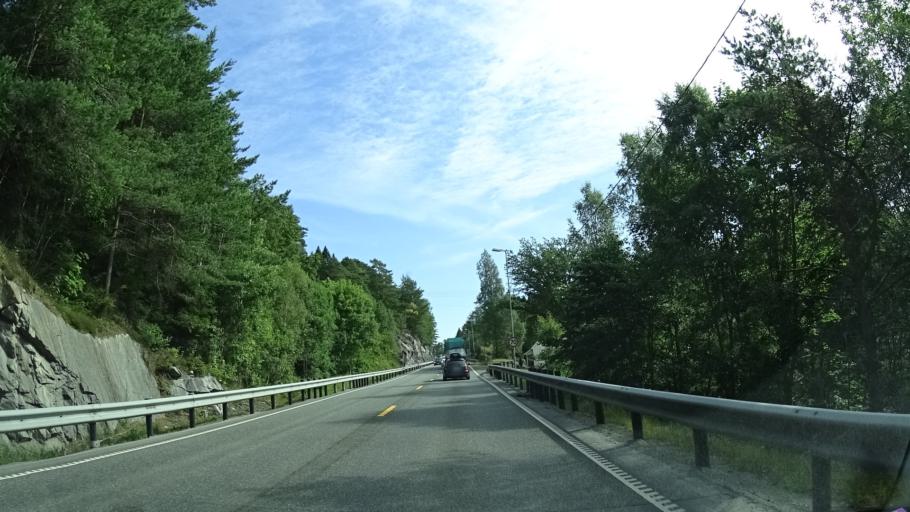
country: NO
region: Telemark
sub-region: Bamble
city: Langesund
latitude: 58.9937
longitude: 9.6406
